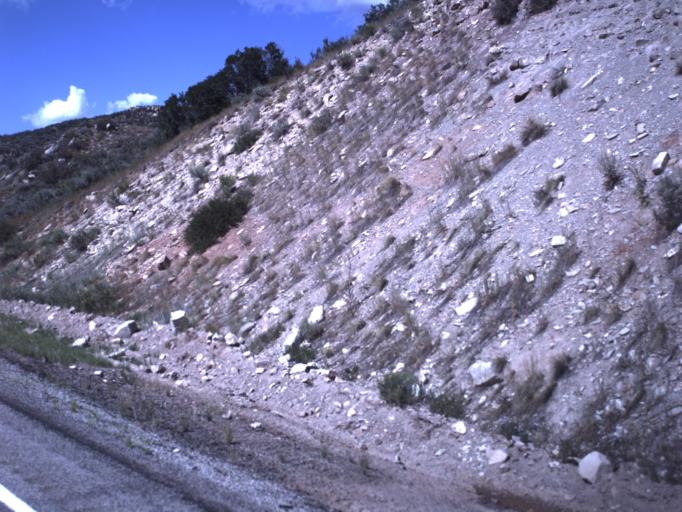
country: US
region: Utah
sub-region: Summit County
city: Francis
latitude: 40.1982
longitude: -110.9677
